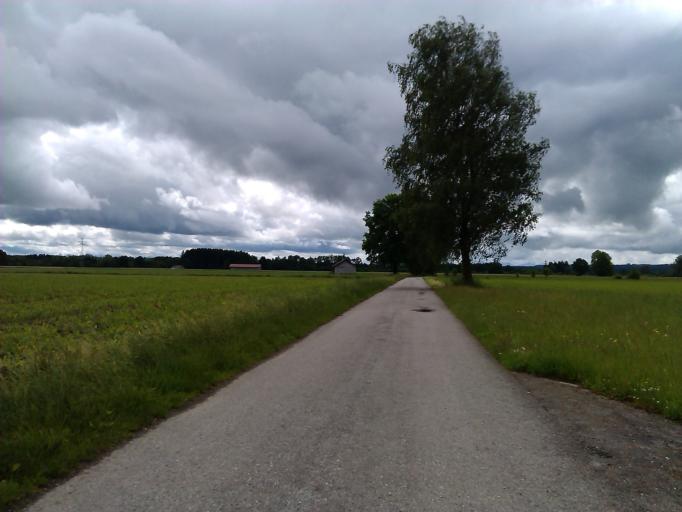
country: DE
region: Bavaria
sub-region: Swabia
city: Pforzen
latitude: 47.9604
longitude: 10.6199
